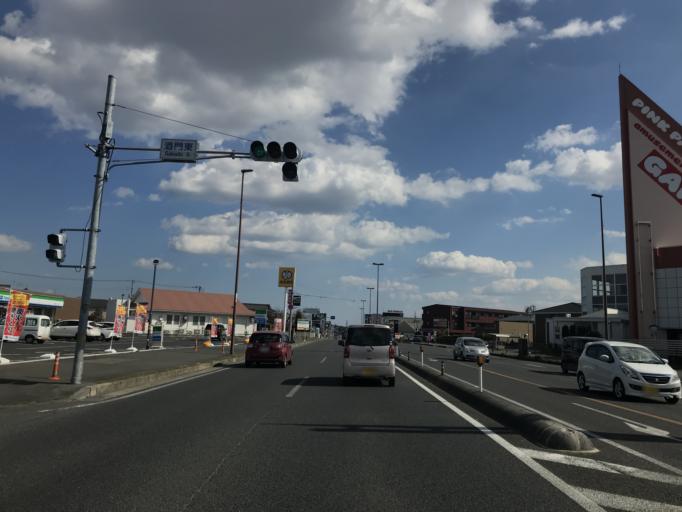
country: JP
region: Ibaraki
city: Mito-shi
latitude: 36.3387
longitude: 140.4835
